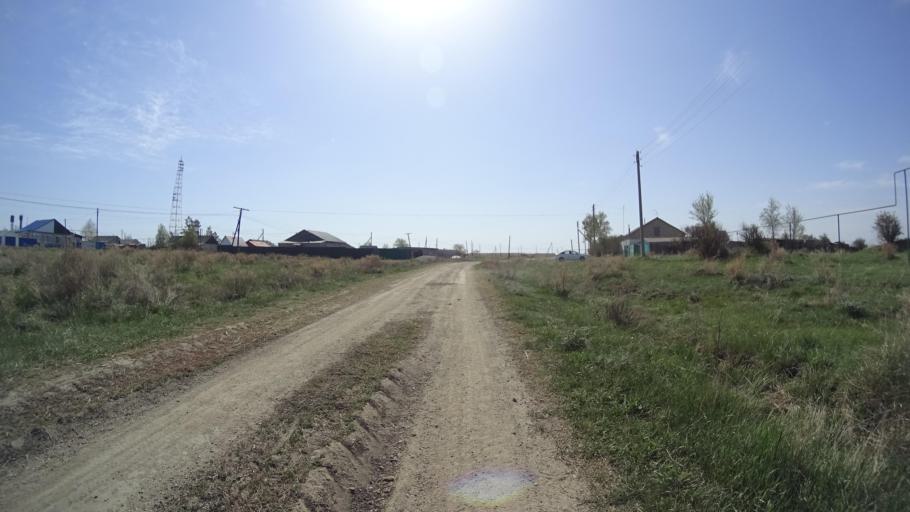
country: RU
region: Chelyabinsk
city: Chesma
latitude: 53.7903
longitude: 61.0369
